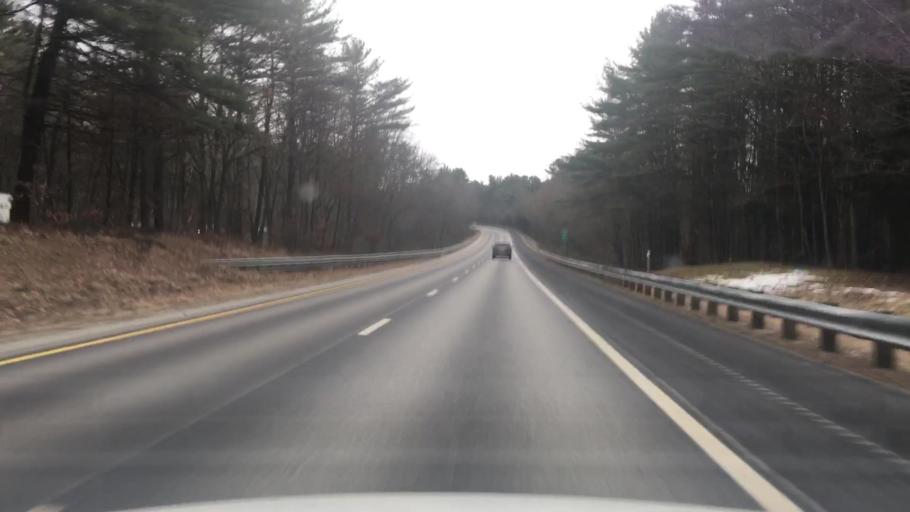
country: US
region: New Hampshire
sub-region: Merrimack County
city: Hopkinton
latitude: 43.1769
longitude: -71.6213
